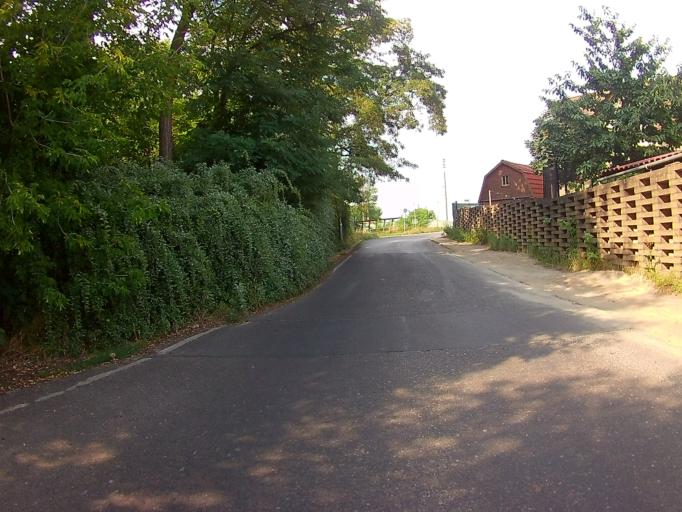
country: DE
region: Berlin
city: Grunau
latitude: 52.4275
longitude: 13.5725
